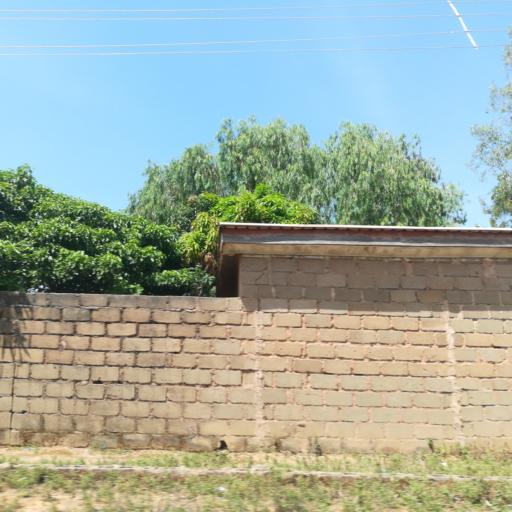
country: NG
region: Plateau
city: Bukuru
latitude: 9.8479
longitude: 8.8788
